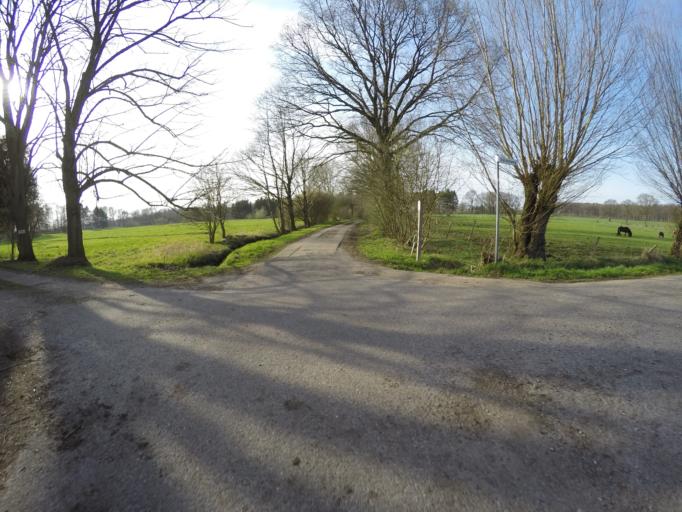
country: DE
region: Schleswig-Holstein
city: Bilsen
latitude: 53.7479
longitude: 9.8732
